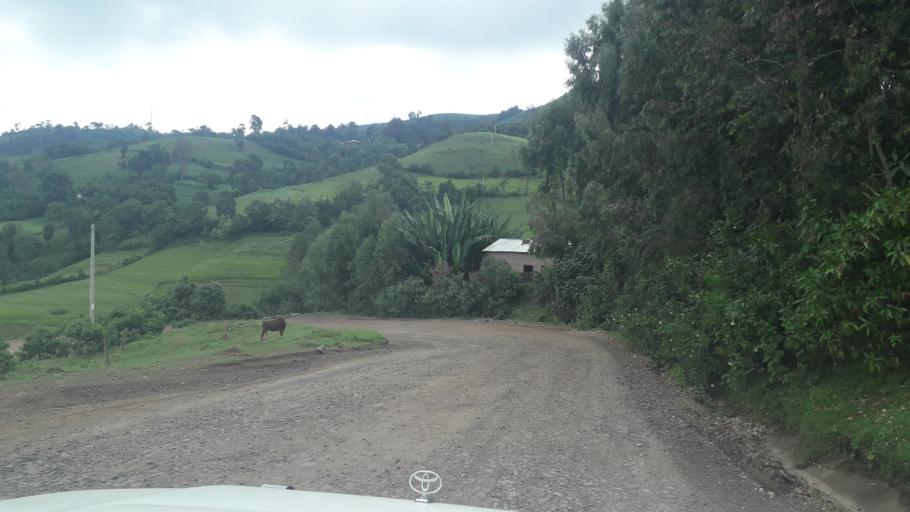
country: ET
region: Oromiya
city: Jima
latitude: 7.4582
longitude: 36.8721
